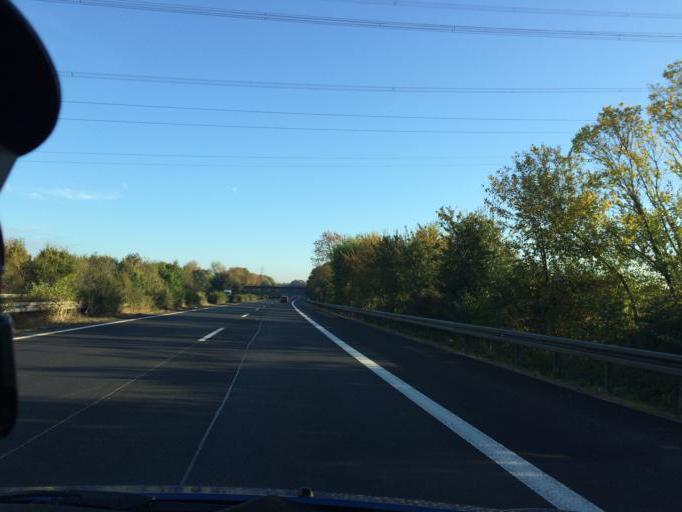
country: DE
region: North Rhine-Westphalia
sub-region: Regierungsbezirk Koln
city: Erftstadt
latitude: 50.8311
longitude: 6.7895
